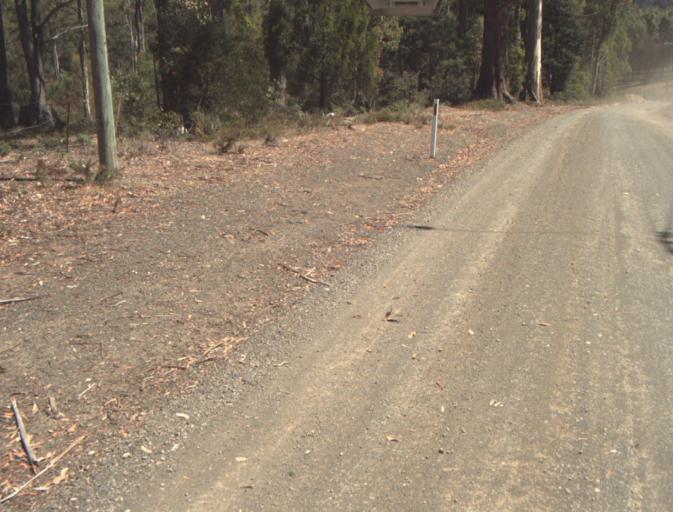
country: AU
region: Tasmania
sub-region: Launceston
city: Newstead
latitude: -41.3433
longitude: 147.3547
